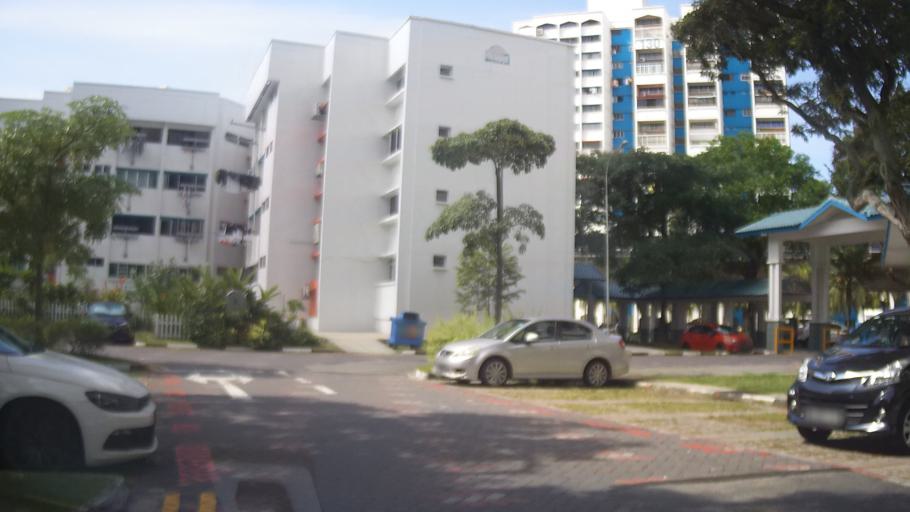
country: SG
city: Singapore
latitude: 1.3182
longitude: 103.8874
